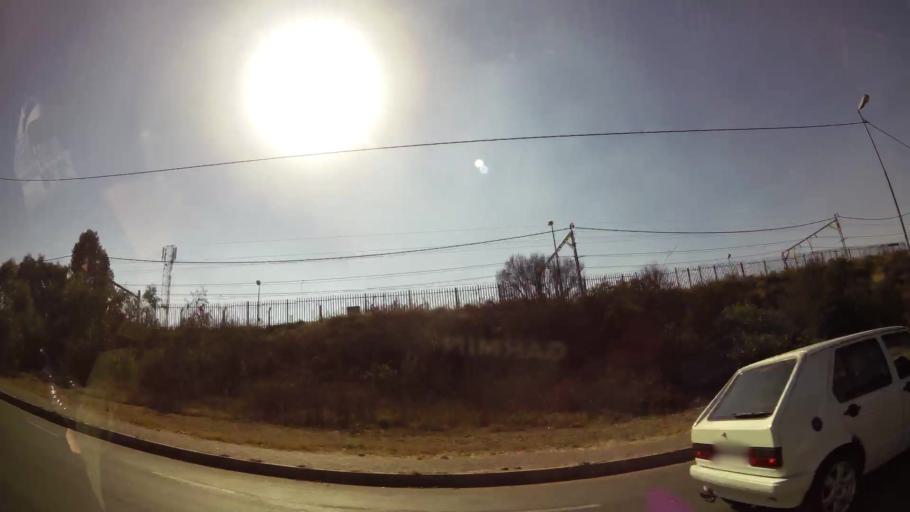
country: ZA
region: Gauteng
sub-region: City of Johannesburg Metropolitan Municipality
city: Johannesburg
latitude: -26.1868
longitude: 27.9633
